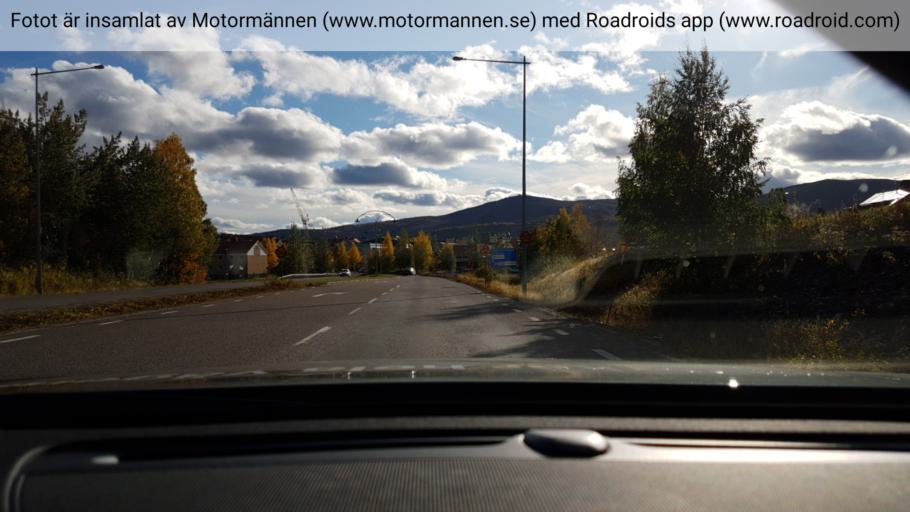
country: SE
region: Norrbotten
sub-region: Gallivare Kommun
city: Gaellivare
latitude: 67.1400
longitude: 20.6617
